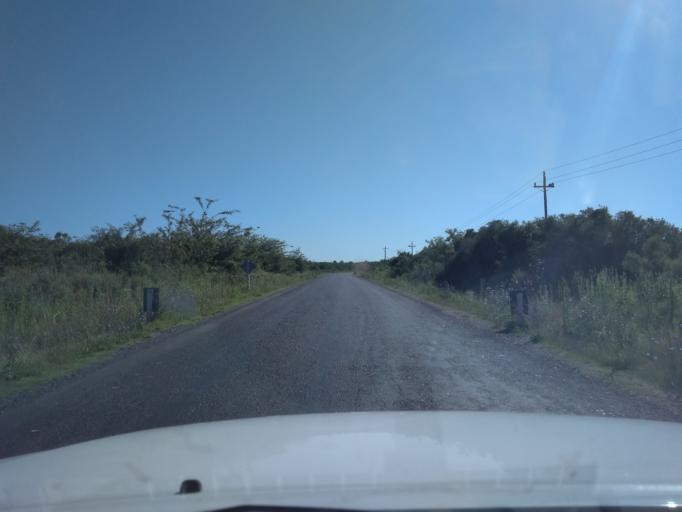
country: UY
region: Canelones
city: San Ramon
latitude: -34.2702
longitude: -55.9414
